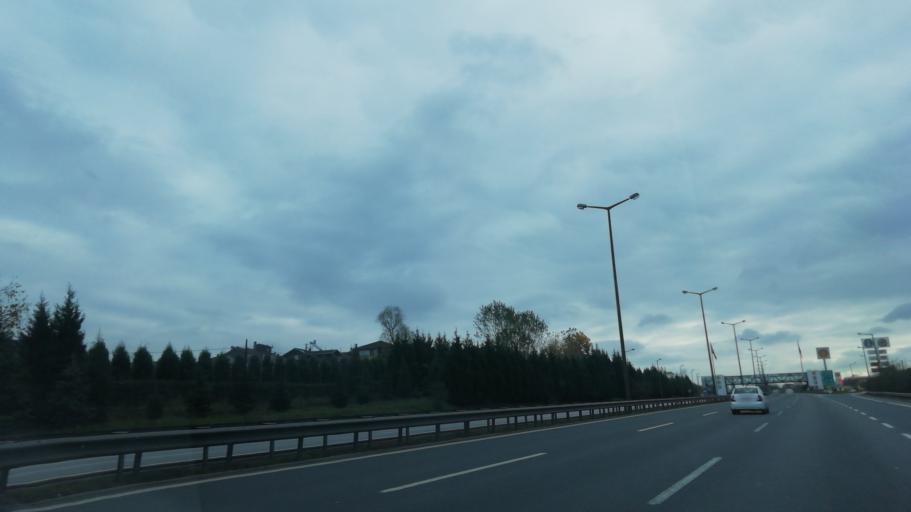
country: TR
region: Kocaeli
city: Derbent
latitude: 40.7288
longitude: 30.0652
